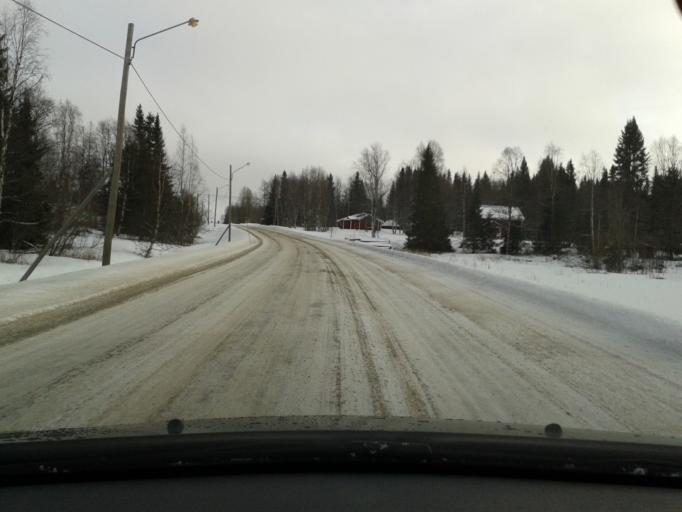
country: SE
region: Vaesterbotten
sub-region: Vilhelmina Kommun
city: Sjoberg
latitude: 64.7936
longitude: 16.0779
